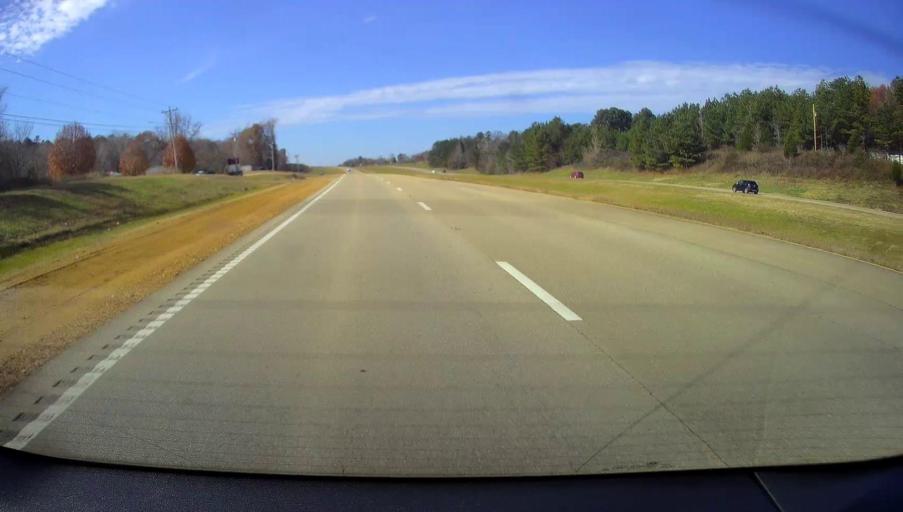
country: US
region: Mississippi
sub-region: Tippah County
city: Ripley
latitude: 34.9542
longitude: -88.9545
